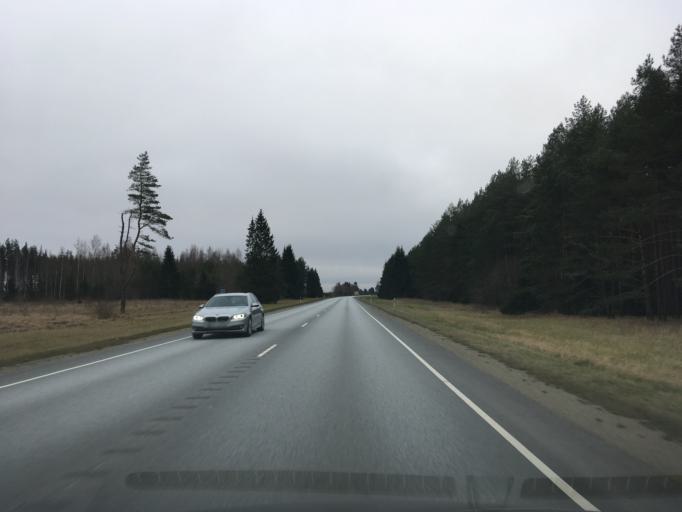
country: EE
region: Laeaene-Virumaa
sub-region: Viru-Nigula vald
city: Kunda
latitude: 59.3966
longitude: 26.6259
